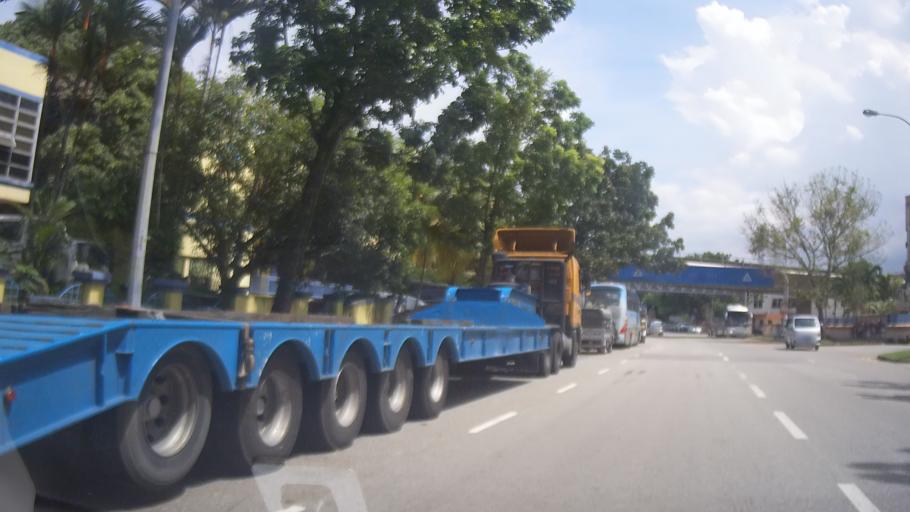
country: MY
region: Johor
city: Johor Bahru
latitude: 1.4067
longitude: 103.7506
